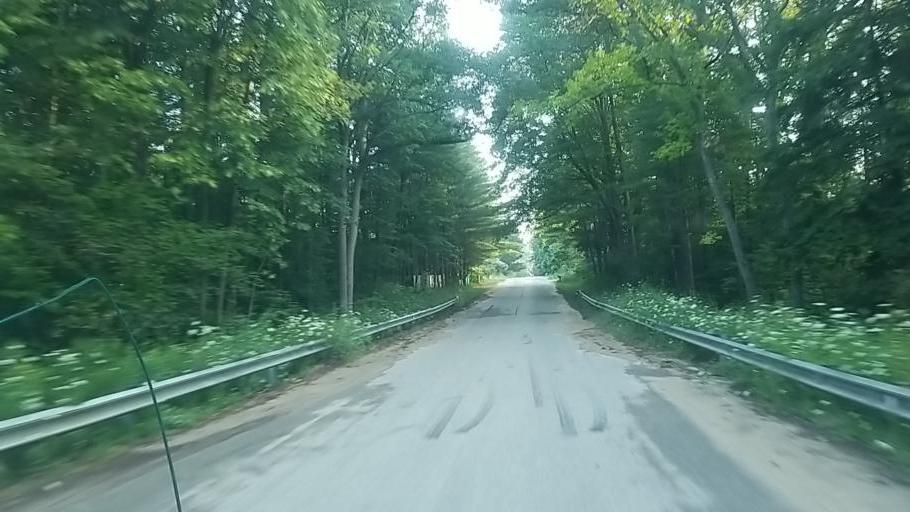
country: US
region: Michigan
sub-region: Muskegon County
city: Twin Lake
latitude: 43.4505
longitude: -86.0990
